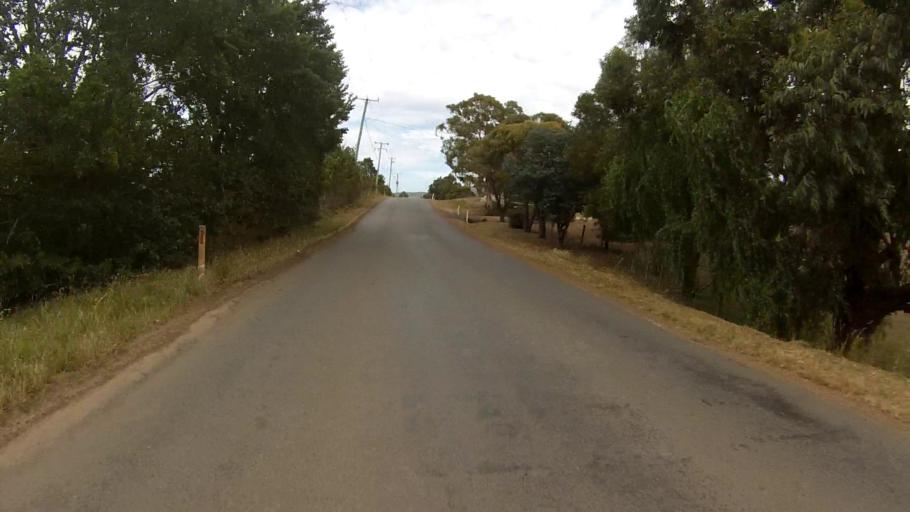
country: AU
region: Tasmania
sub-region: Clarence
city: Cambridge
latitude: -42.7302
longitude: 147.4488
